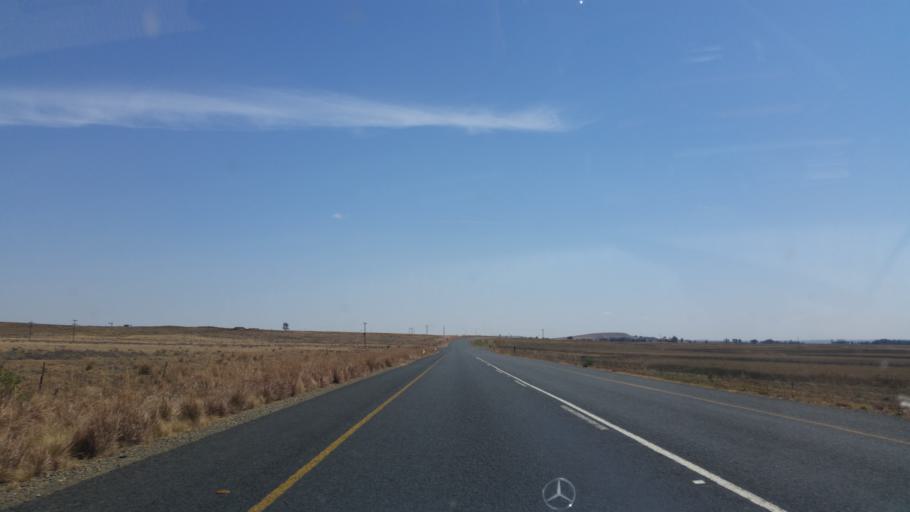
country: ZA
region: Orange Free State
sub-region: Thabo Mofutsanyana District Municipality
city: Phuthaditjhaba
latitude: -28.2546
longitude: 28.7188
